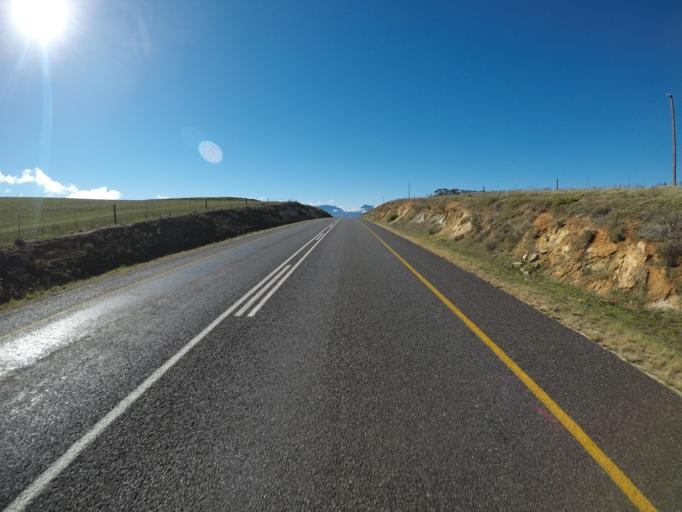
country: ZA
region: Western Cape
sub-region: Overberg District Municipality
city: Caledon
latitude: -34.1425
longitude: 19.5000
